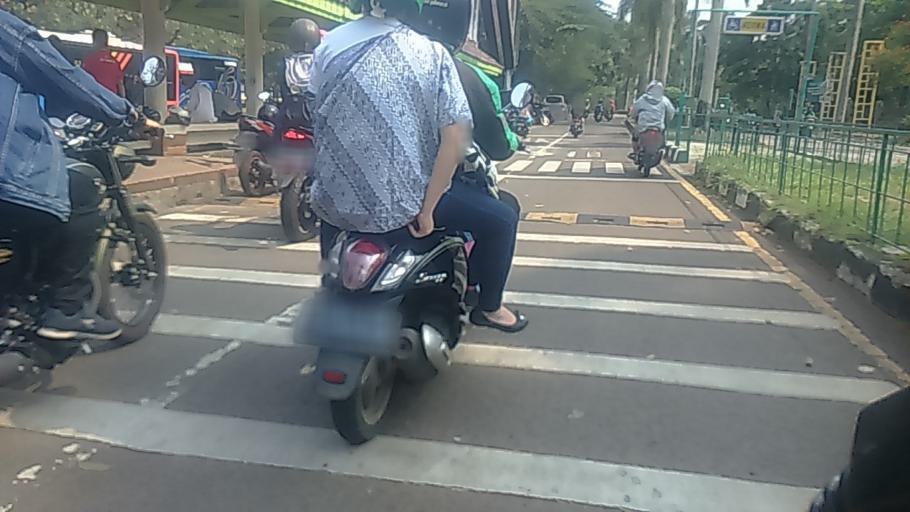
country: ID
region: West Java
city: Depok
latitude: -6.3542
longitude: 106.8333
